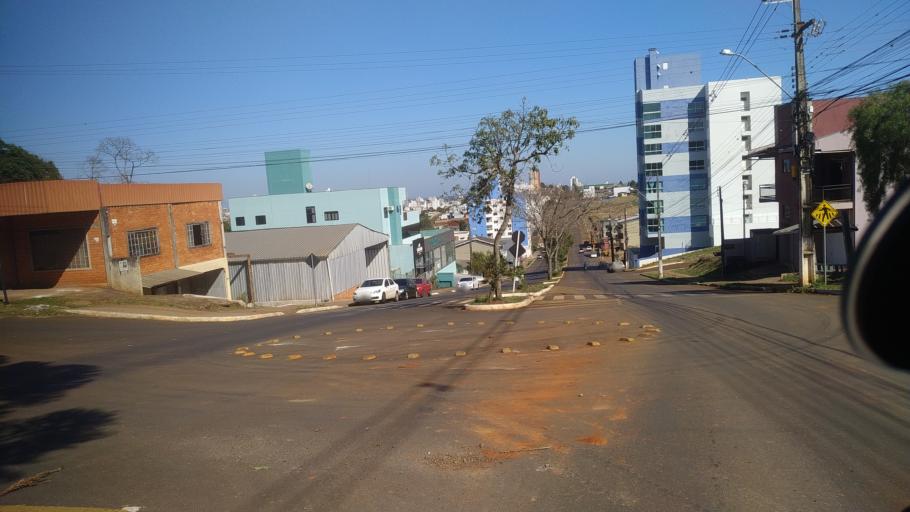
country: BR
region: Santa Catarina
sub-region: Chapeco
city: Chapeco
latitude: -27.0888
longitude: -52.5879
